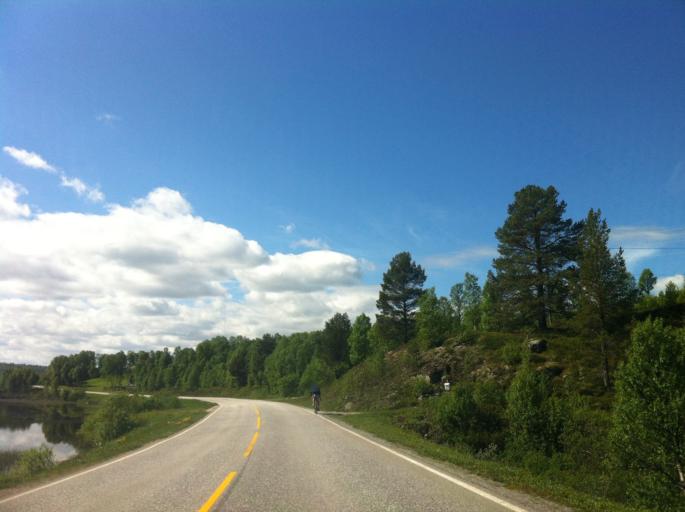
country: NO
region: Sor-Trondelag
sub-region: Roros
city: Roros
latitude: 62.5980
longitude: 11.4689
